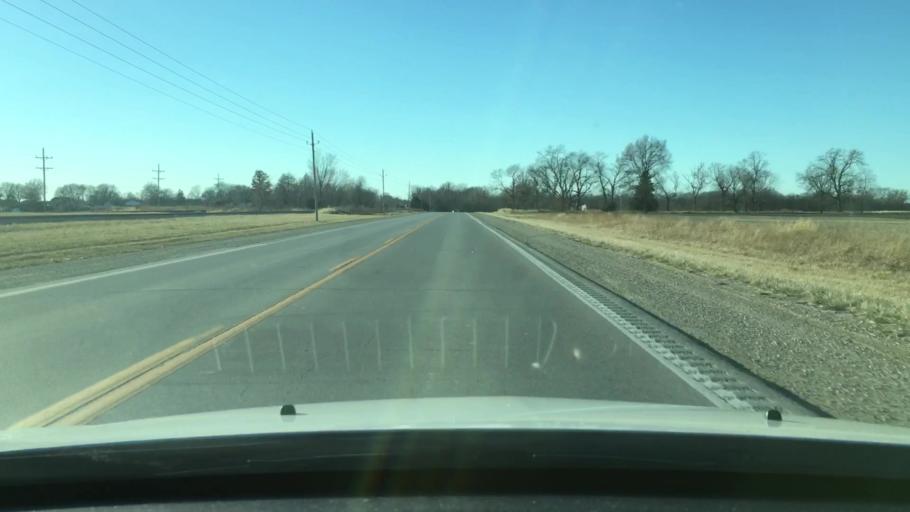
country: US
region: Missouri
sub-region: Audrain County
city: Mexico
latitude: 39.1885
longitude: -91.9732
